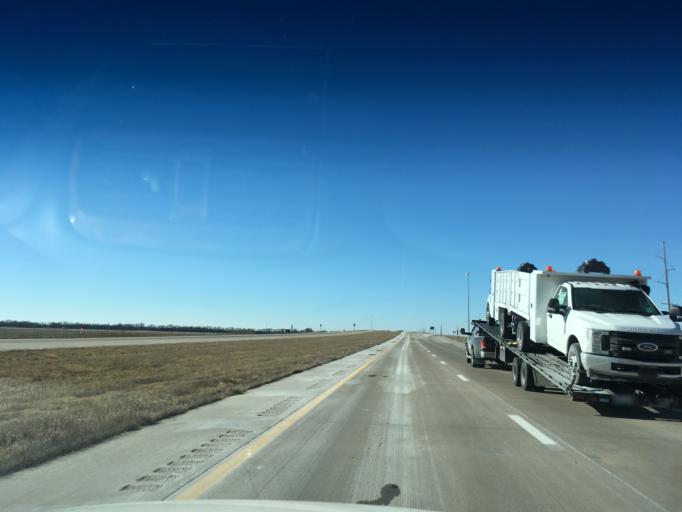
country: US
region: Kansas
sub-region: Reno County
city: Hutchinson
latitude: 38.0288
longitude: -97.8600
